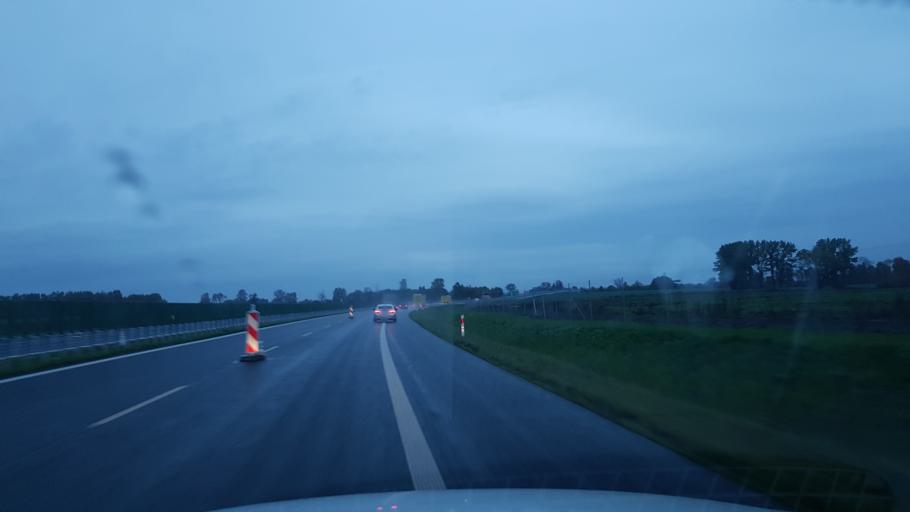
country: PL
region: West Pomeranian Voivodeship
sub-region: Powiat gryficki
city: Ploty
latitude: 53.8057
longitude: 15.2492
